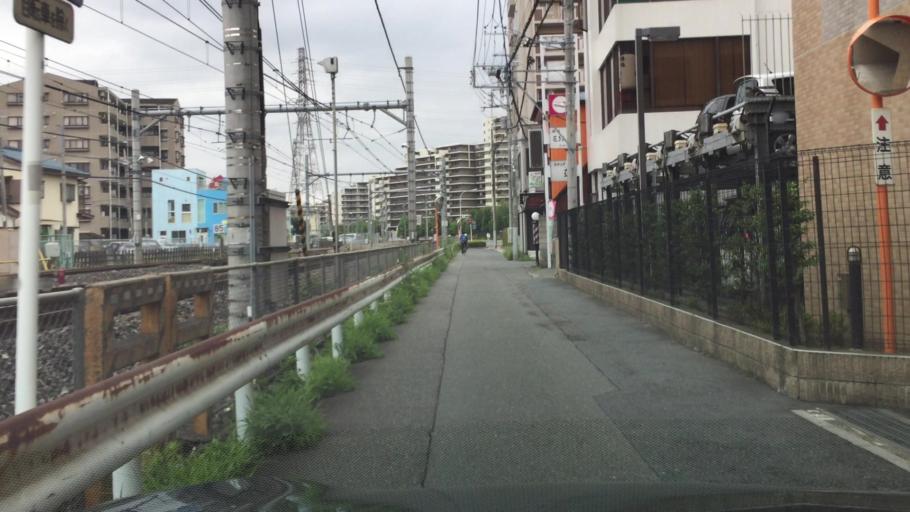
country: JP
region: Saitama
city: Ageoshimo
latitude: 35.9384
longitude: 139.6097
